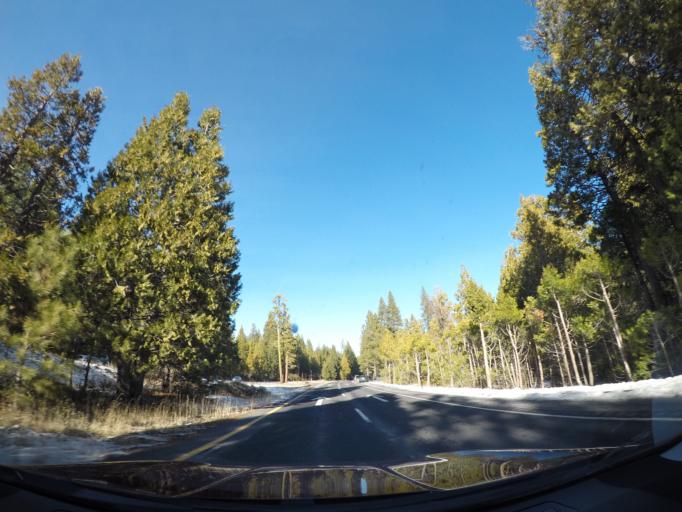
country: US
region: California
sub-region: Tuolumne County
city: Twain Harte
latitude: 38.1112
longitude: -120.1224
